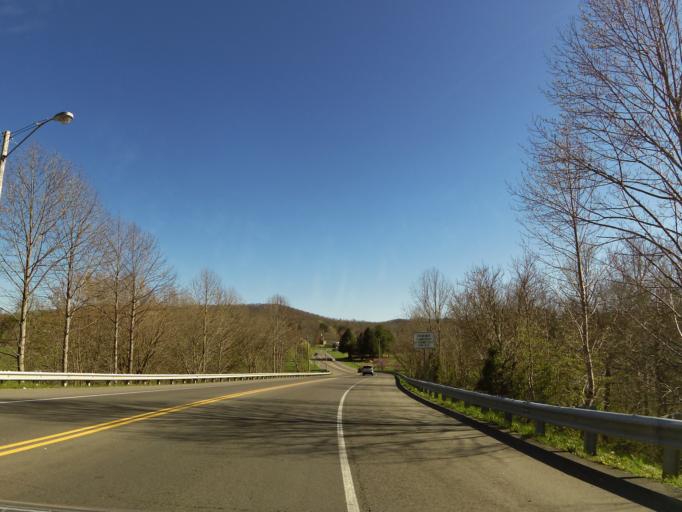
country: US
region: Tennessee
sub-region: Scott County
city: Oneida
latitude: 36.4987
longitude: -84.5081
